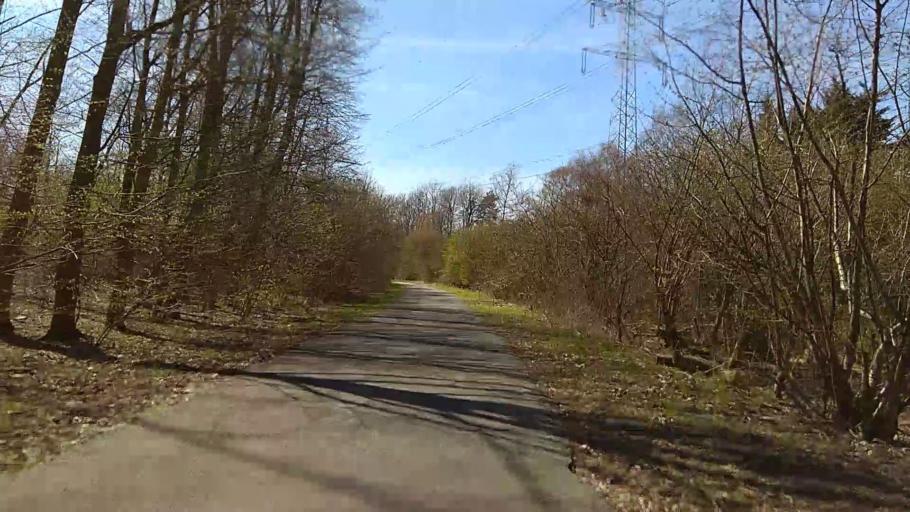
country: DE
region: North Rhine-Westphalia
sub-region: Regierungsbezirk Munster
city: Gladbeck
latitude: 51.5809
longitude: 7.0243
